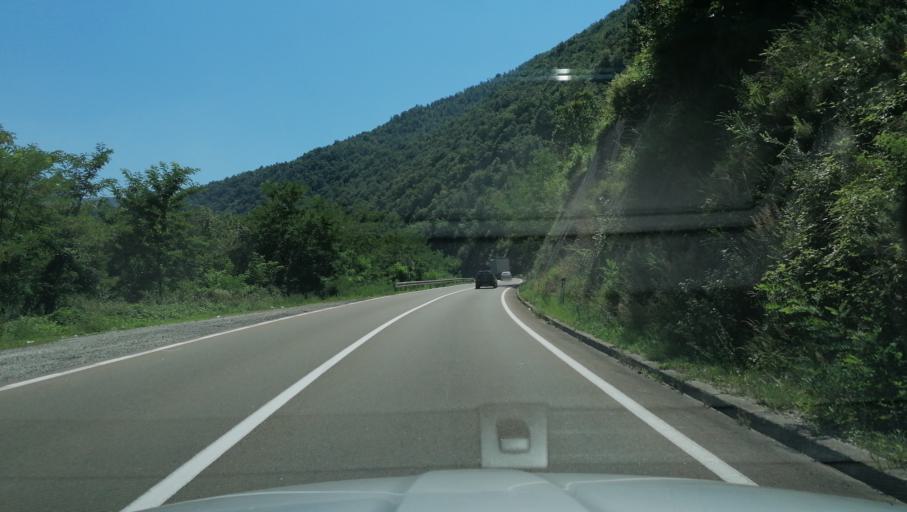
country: RS
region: Central Serbia
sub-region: Raski Okrug
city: Kraljevo
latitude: 43.5663
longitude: 20.6023
